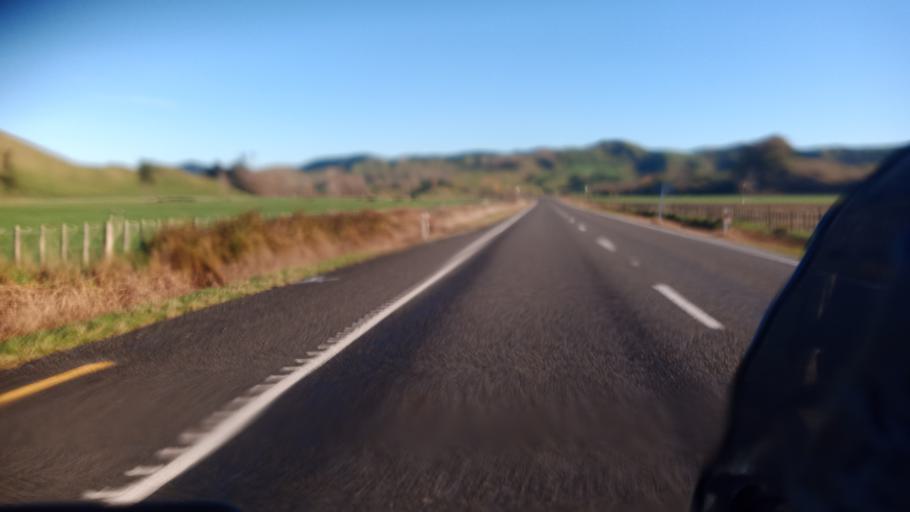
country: NZ
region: Hawke's Bay
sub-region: Wairoa District
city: Wairoa
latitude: -39.0191
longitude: 177.3724
